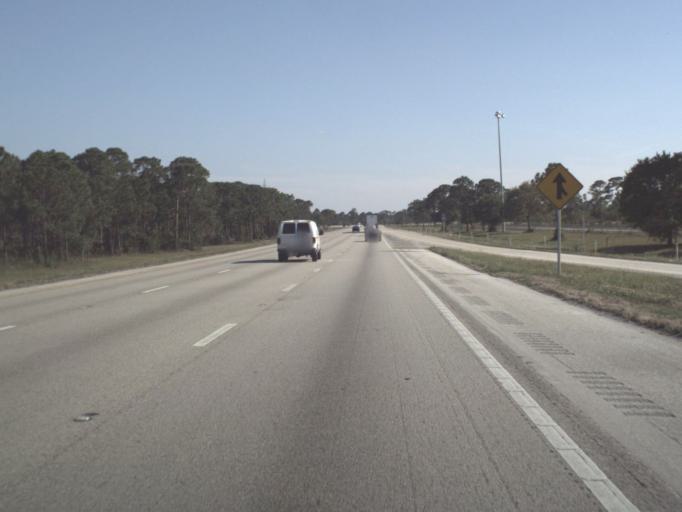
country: US
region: Florida
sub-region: Martin County
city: Palm City
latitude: 27.1584
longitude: -80.3893
